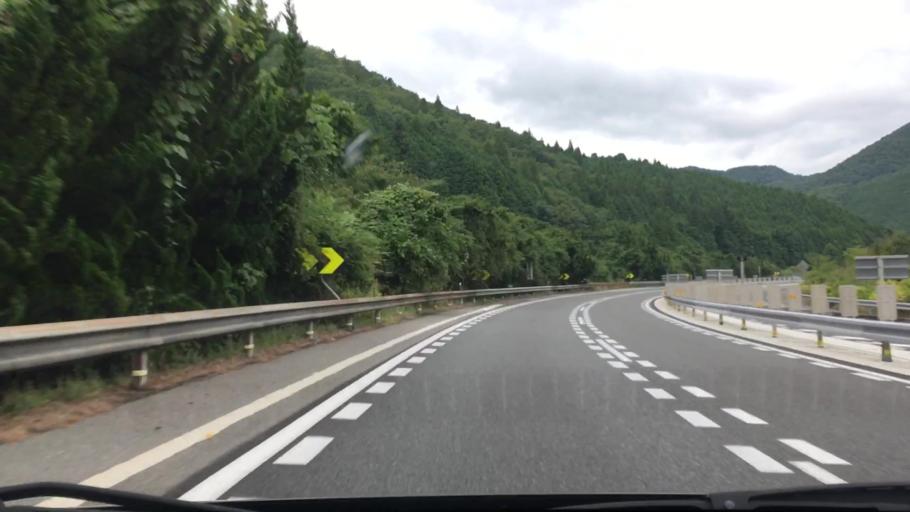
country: JP
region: Okayama
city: Niimi
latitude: 35.0056
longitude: 133.4878
